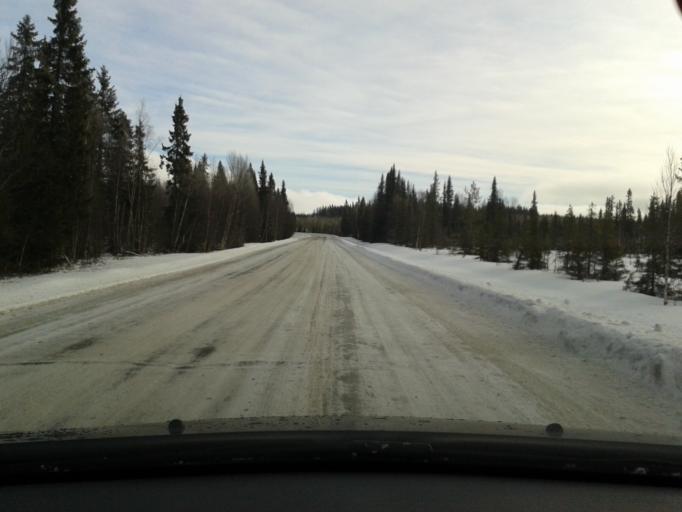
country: SE
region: Vaesterbotten
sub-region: Vilhelmina Kommun
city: Sjoberg
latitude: 64.7462
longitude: 16.1774
